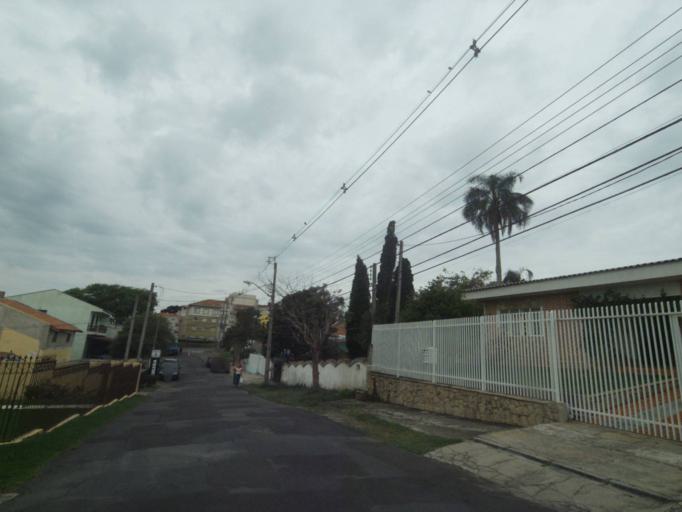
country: BR
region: Parana
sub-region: Curitiba
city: Curitiba
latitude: -25.3932
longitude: -49.2969
